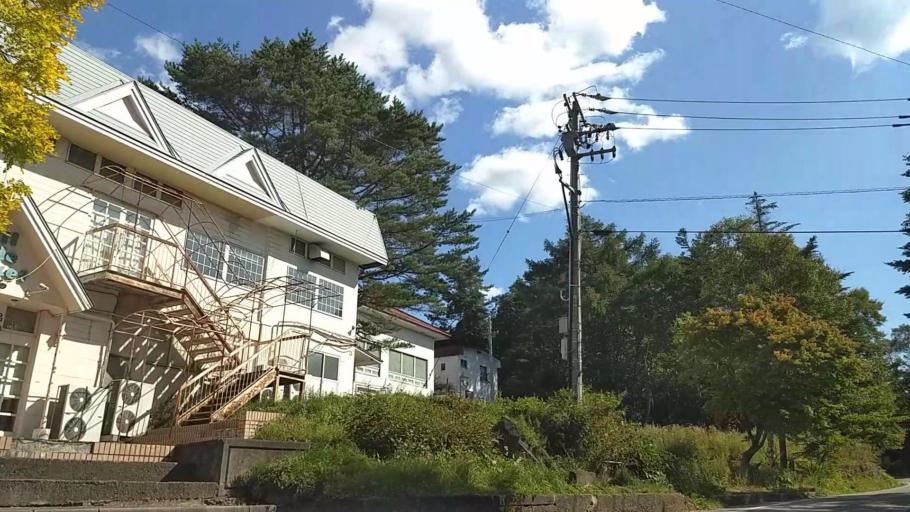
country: JP
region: Nagano
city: Chino
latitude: 36.1289
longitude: 138.2718
